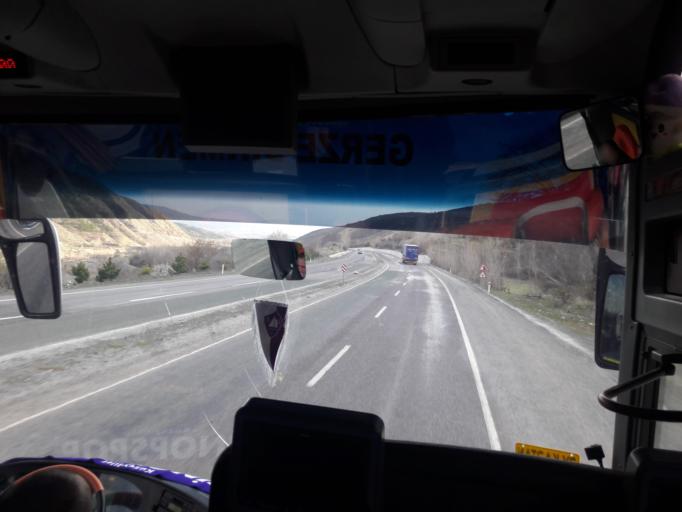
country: TR
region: Cankiri
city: Korgun
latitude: 40.7609
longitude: 33.5271
